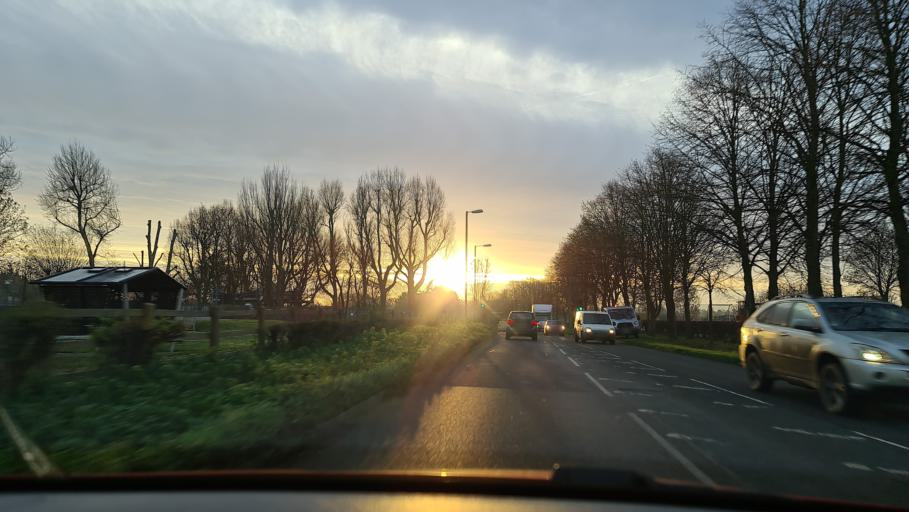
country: GB
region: England
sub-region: Oxfordshire
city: Thame
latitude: 51.7541
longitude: -0.9744
